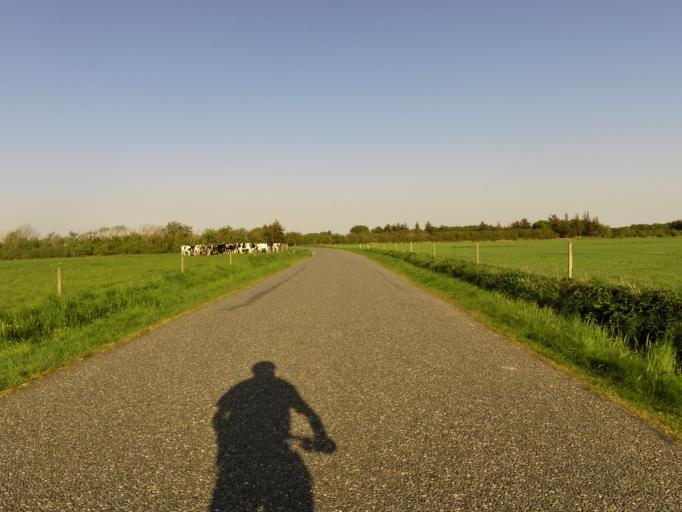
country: DK
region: South Denmark
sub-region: Esbjerg Kommune
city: Ribe
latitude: 55.2954
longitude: 8.6598
